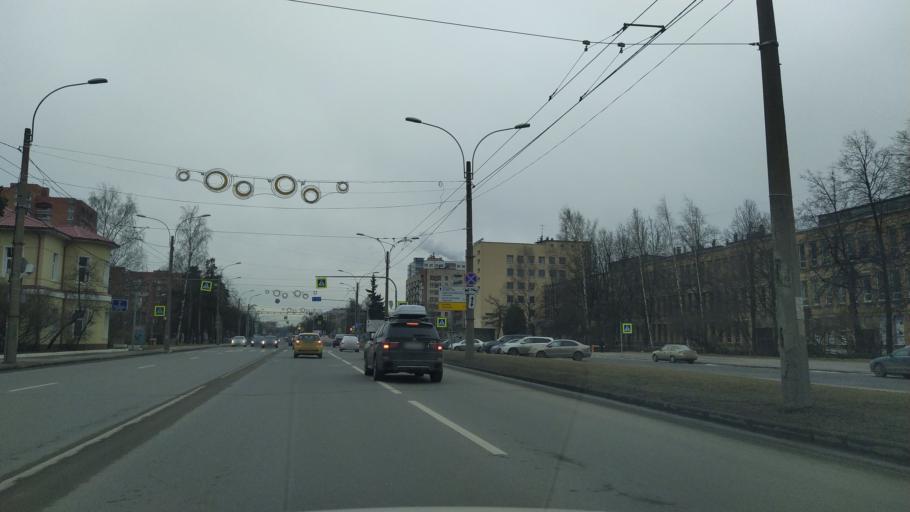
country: RU
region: St.-Petersburg
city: Sosnovka
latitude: 60.0122
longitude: 30.3448
